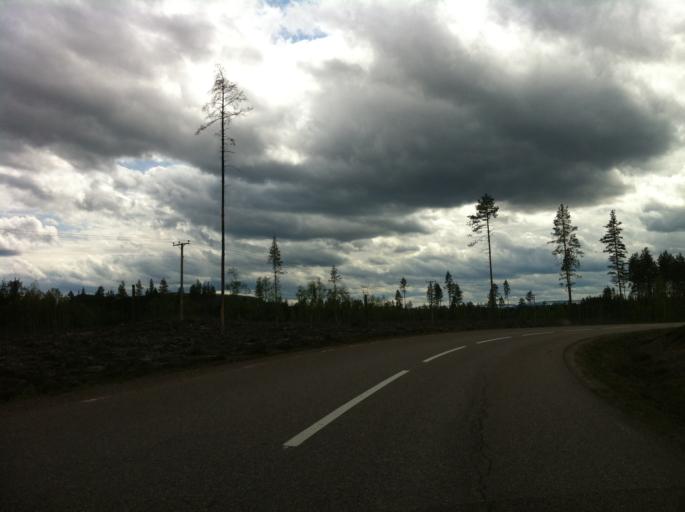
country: NO
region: Hedmark
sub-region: Trysil
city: Innbygda
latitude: 61.4322
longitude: 13.0962
